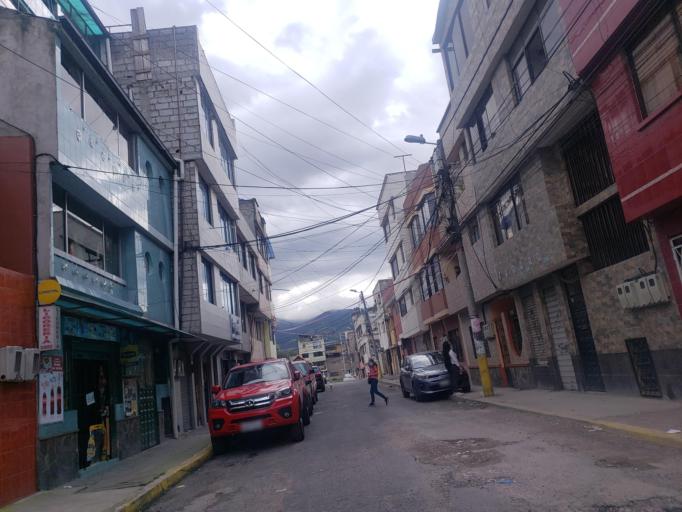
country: EC
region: Pichincha
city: Quito
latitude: -0.2692
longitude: -78.5424
